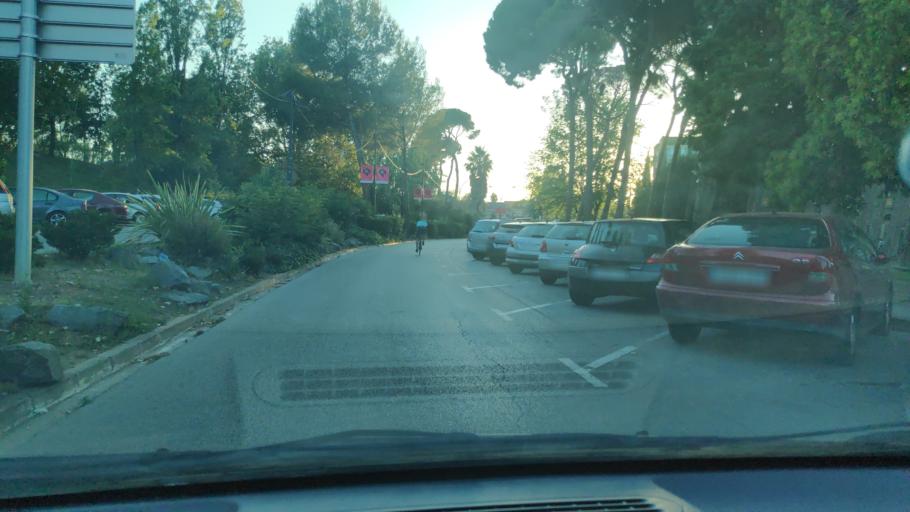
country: ES
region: Catalonia
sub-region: Provincia de Barcelona
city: Cerdanyola del Valles
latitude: 41.4890
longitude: 2.1473
